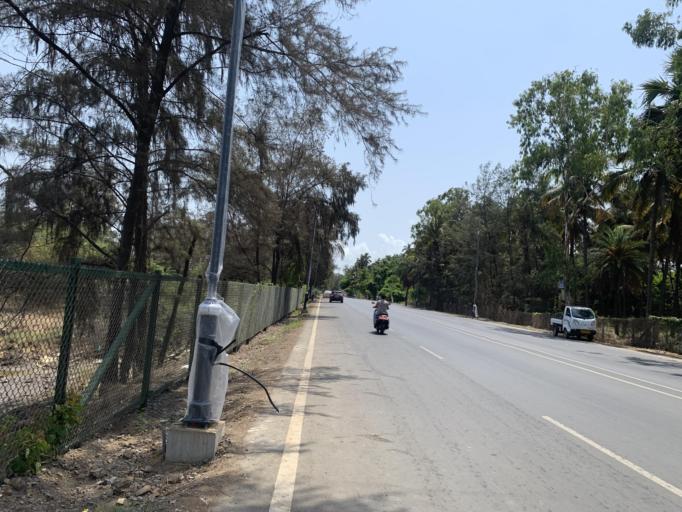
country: IN
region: Daman and Diu
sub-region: Daman District
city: Daman
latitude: 20.4605
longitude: 72.8475
